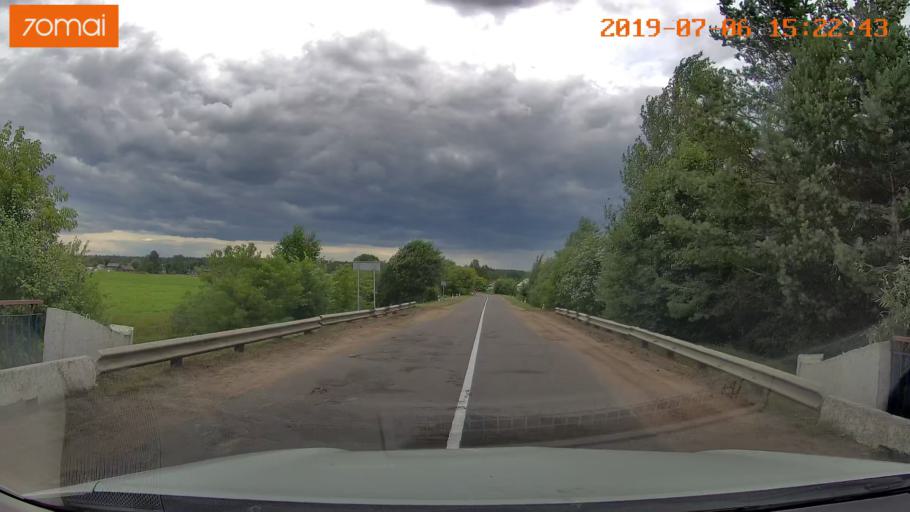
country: BY
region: Minsk
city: Valozhyn
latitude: 54.0143
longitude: 26.6054
